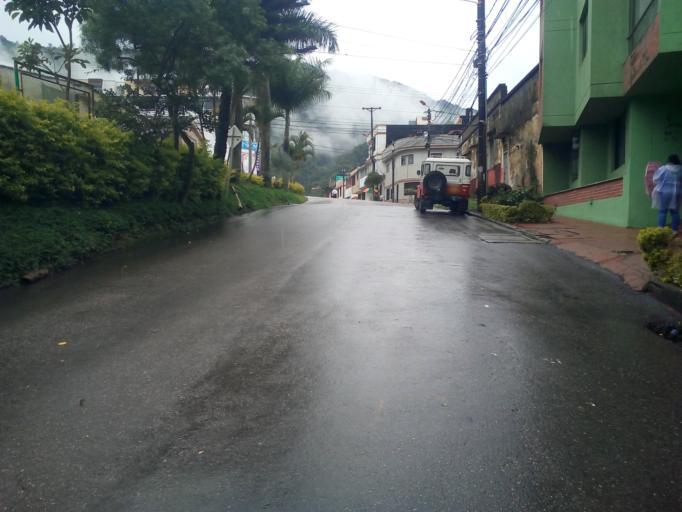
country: CO
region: Tolima
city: Ibague
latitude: 4.4511
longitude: -75.2459
